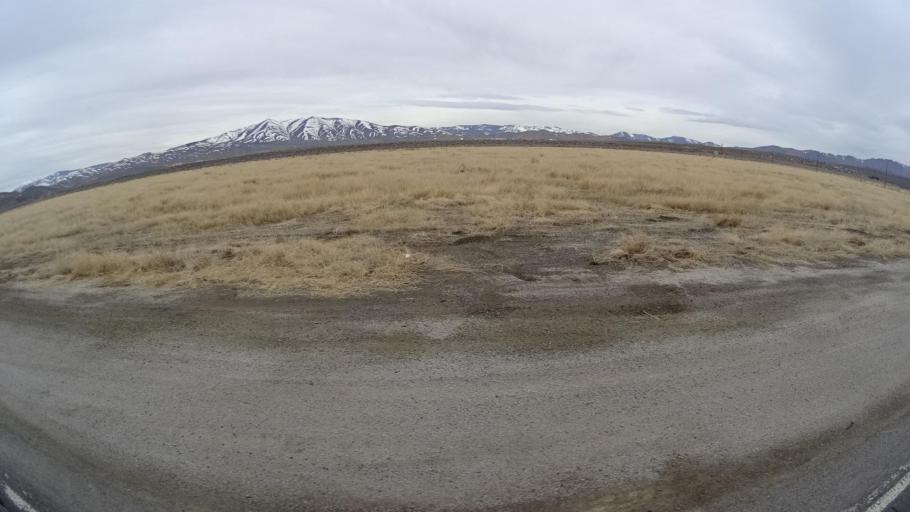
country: US
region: Nevada
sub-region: Washoe County
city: Lemmon Valley
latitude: 39.6636
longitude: -119.8293
